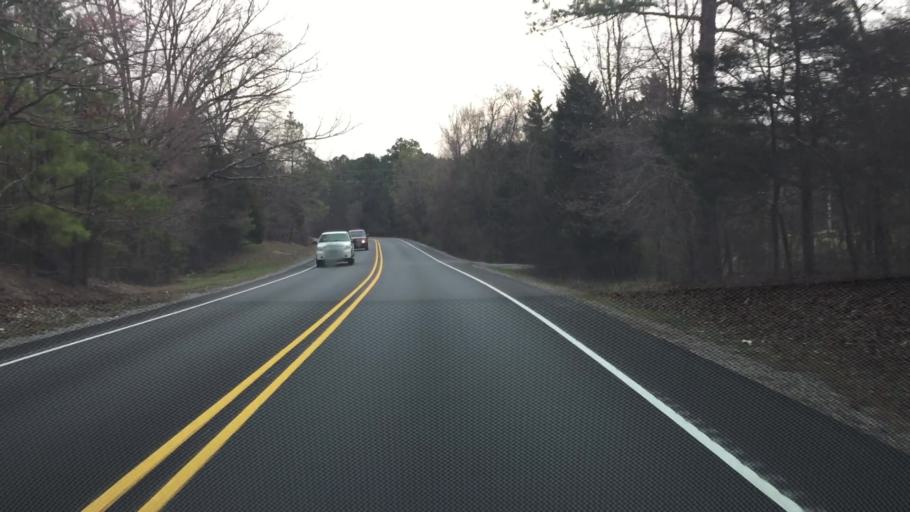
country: US
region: Arkansas
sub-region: Saline County
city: Haskell
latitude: 34.6118
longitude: -92.8028
